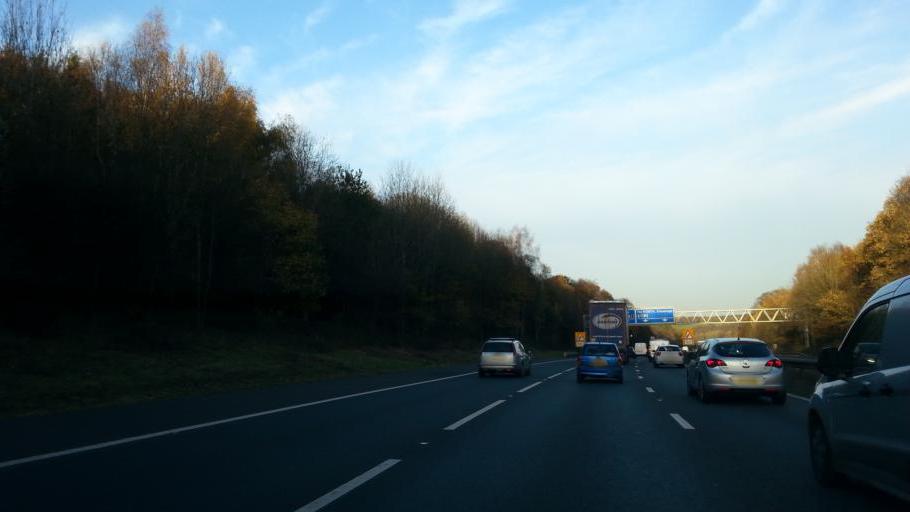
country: GB
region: England
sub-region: Hertfordshire
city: Welwyn
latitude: 51.8148
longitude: -0.2251
